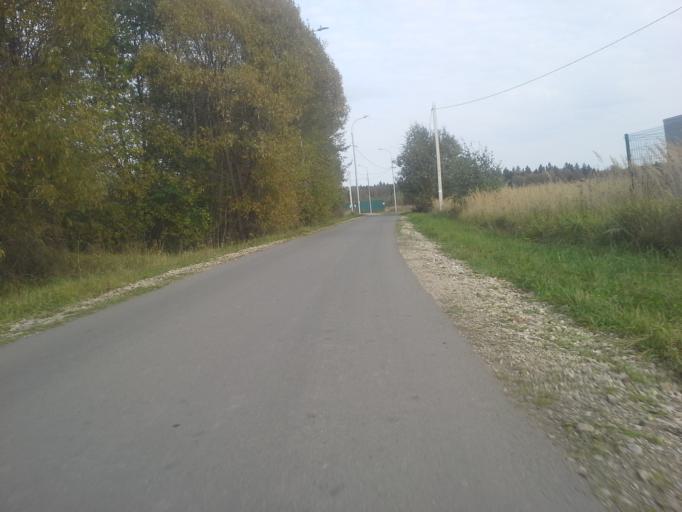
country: RU
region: Moskovskaya
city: Kievskij
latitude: 55.3970
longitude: 36.9101
